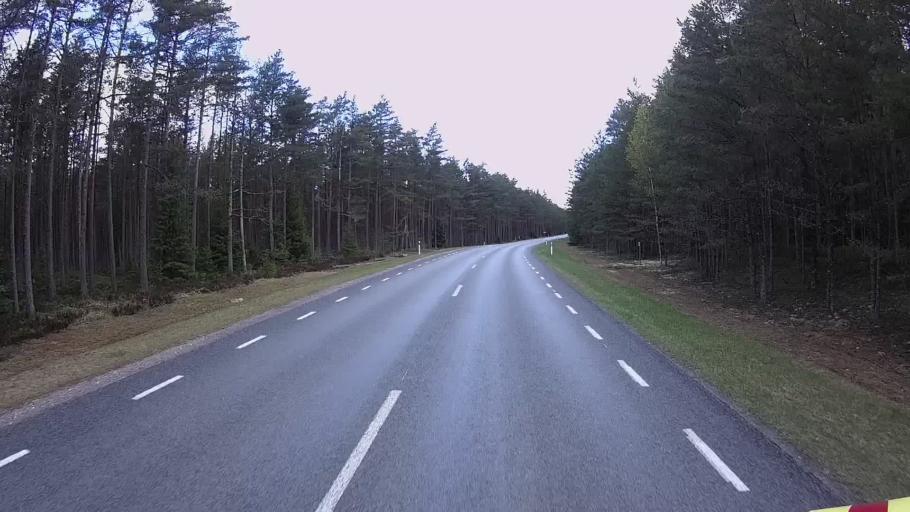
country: EE
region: Hiiumaa
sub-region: Kaerdla linn
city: Kardla
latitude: 58.9284
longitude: 22.7850
